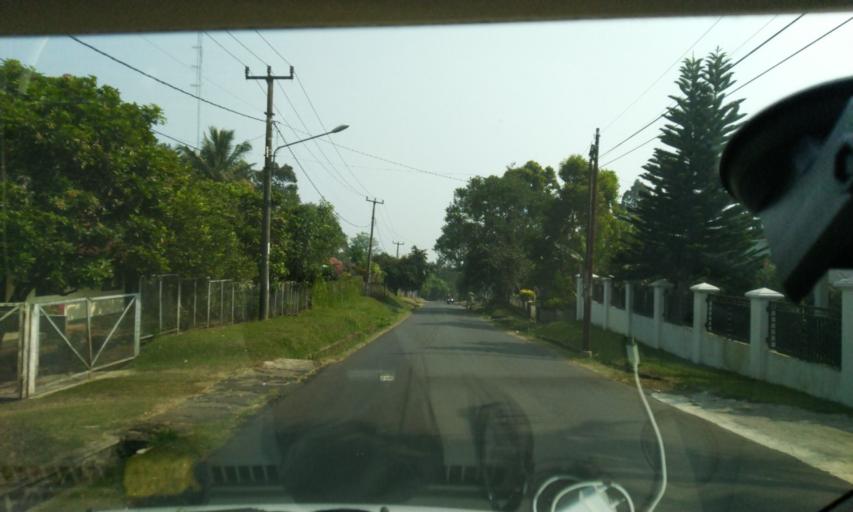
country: ID
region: West Java
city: Caringin
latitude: -6.6633
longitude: 106.8624
